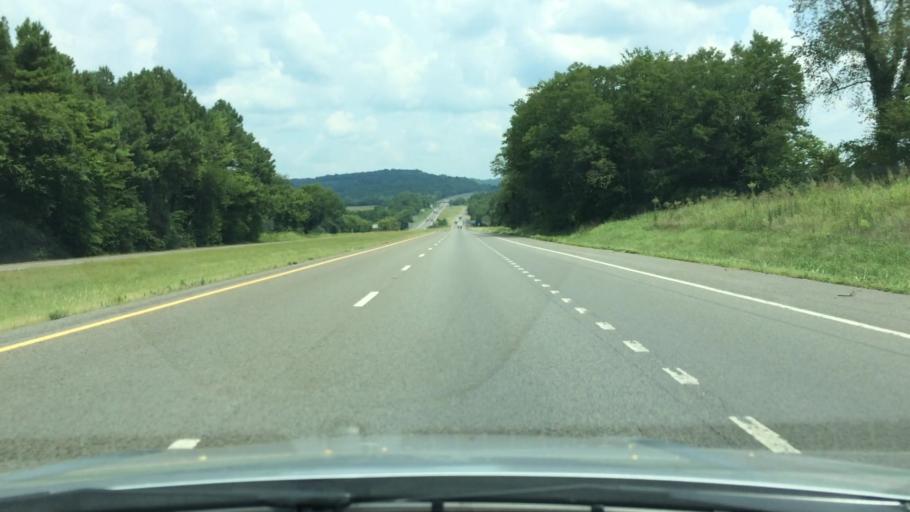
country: US
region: Tennessee
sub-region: Marshall County
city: Cornersville
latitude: 35.3122
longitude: -86.8822
